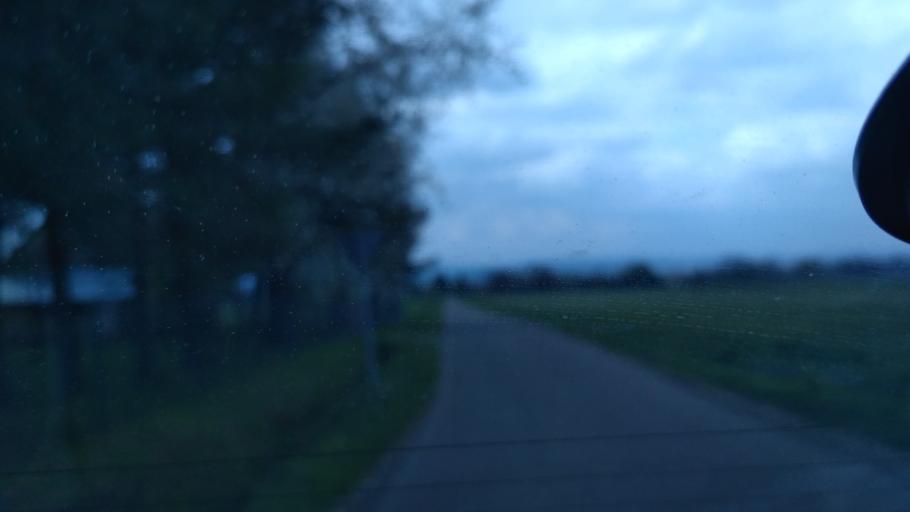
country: PL
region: Subcarpathian Voivodeship
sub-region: Powiat brzozowski
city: Turze Pole
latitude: 49.6283
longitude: 22.0094
